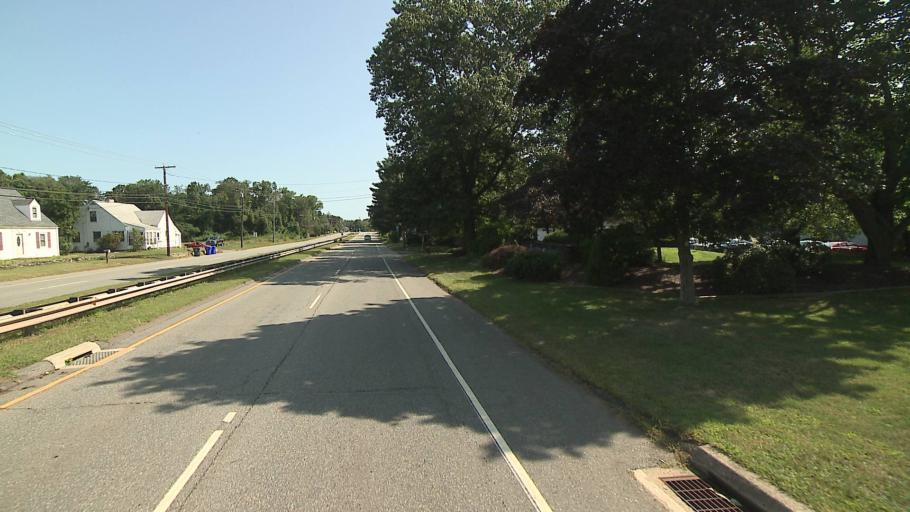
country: US
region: Connecticut
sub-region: Hartford County
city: East Hartford
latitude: 41.7928
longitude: -72.6254
